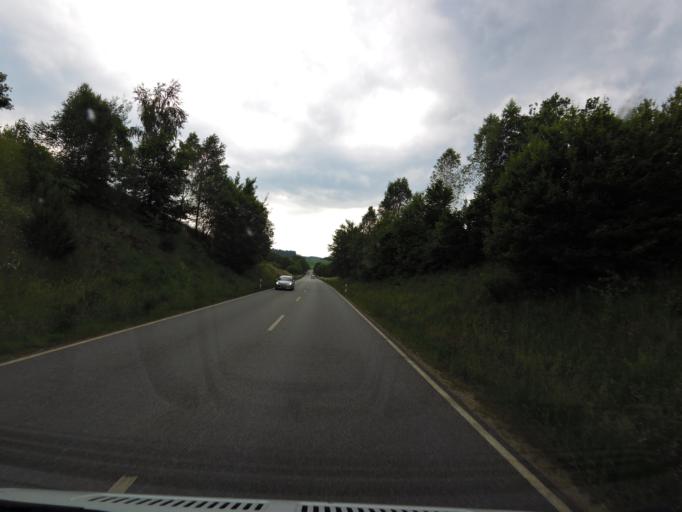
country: DE
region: Bavaria
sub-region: Lower Bavaria
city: Neukirchen vorm Wald
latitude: 48.6876
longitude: 13.3708
